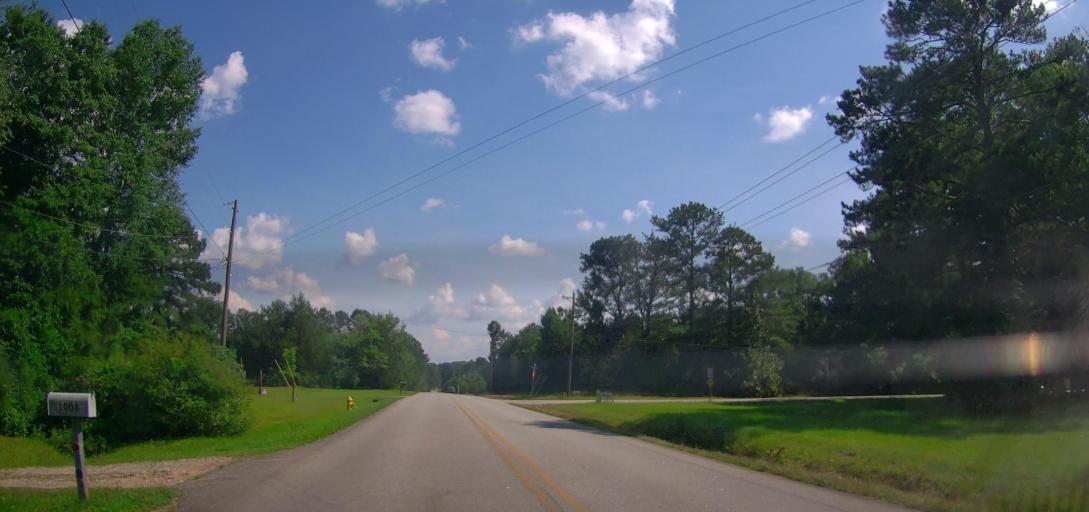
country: US
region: Georgia
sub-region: Spalding County
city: East Griffin
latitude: 33.2728
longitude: -84.1900
